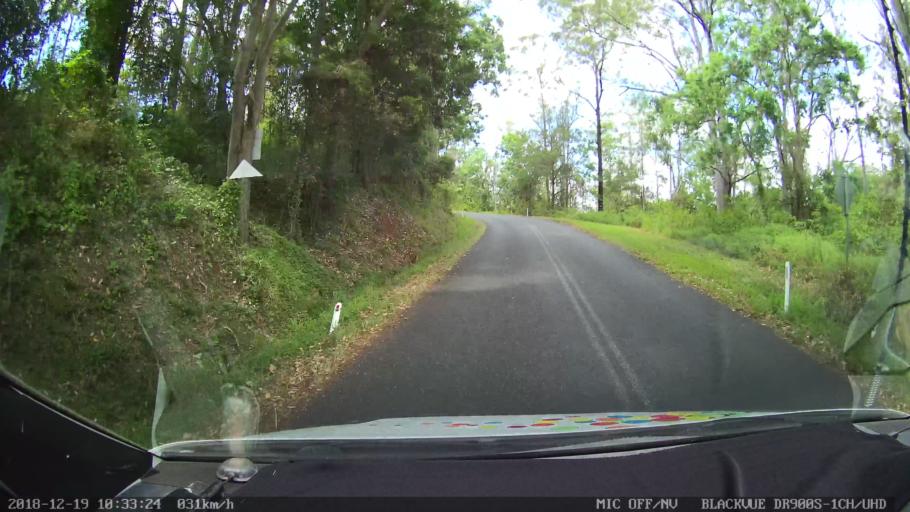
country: AU
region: New South Wales
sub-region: Lismore Municipality
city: Larnook
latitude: -28.5769
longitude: 153.1262
